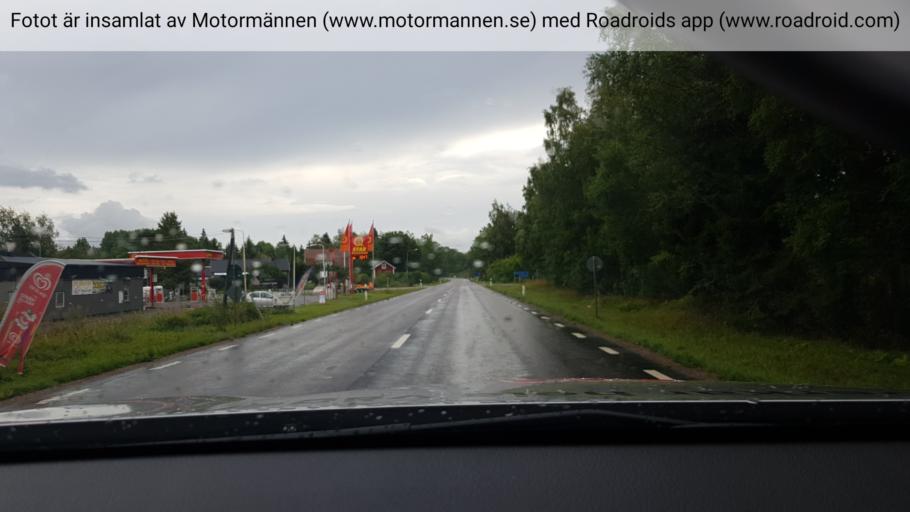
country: SE
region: Uppsala
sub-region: Tierps Kommun
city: Karlholmsbruk
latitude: 60.5247
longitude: 17.6010
